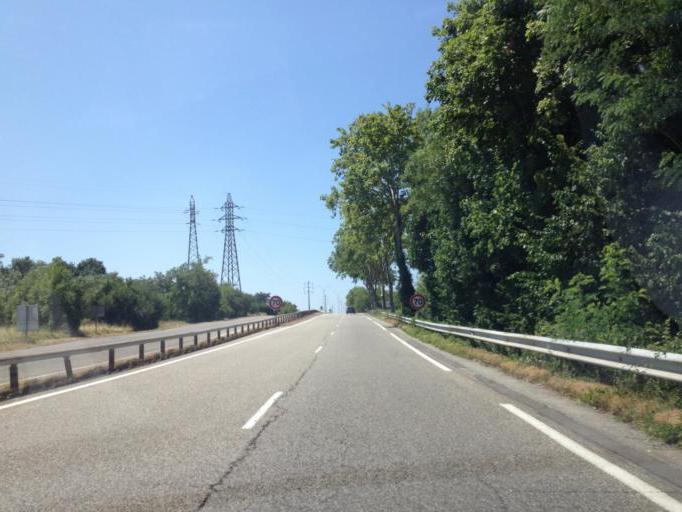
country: FR
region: Rhone-Alpes
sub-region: Departement de la Drome
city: Bourg-les-Valence
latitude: 44.9479
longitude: 4.9247
